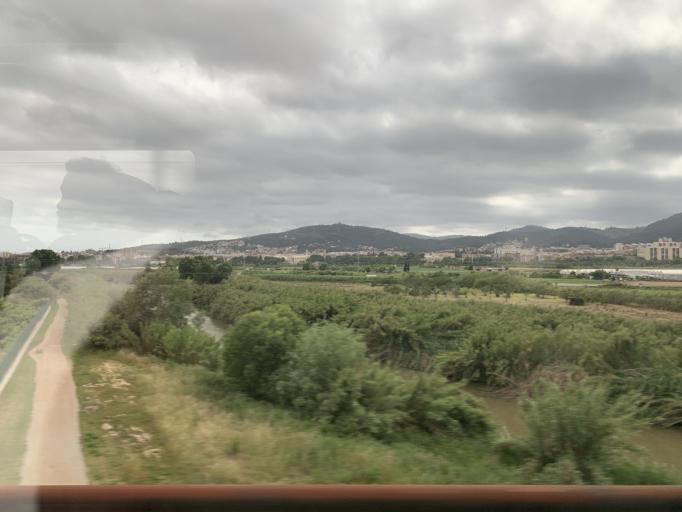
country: ES
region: Catalonia
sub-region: Provincia de Barcelona
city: Sant Boi de Llobregat
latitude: 41.3581
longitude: 2.0482
